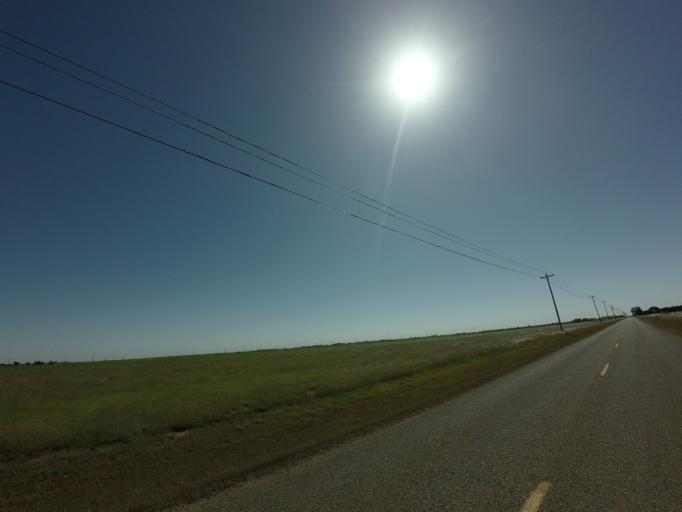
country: US
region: New Mexico
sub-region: Curry County
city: Clovis
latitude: 34.4326
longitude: -103.1608
